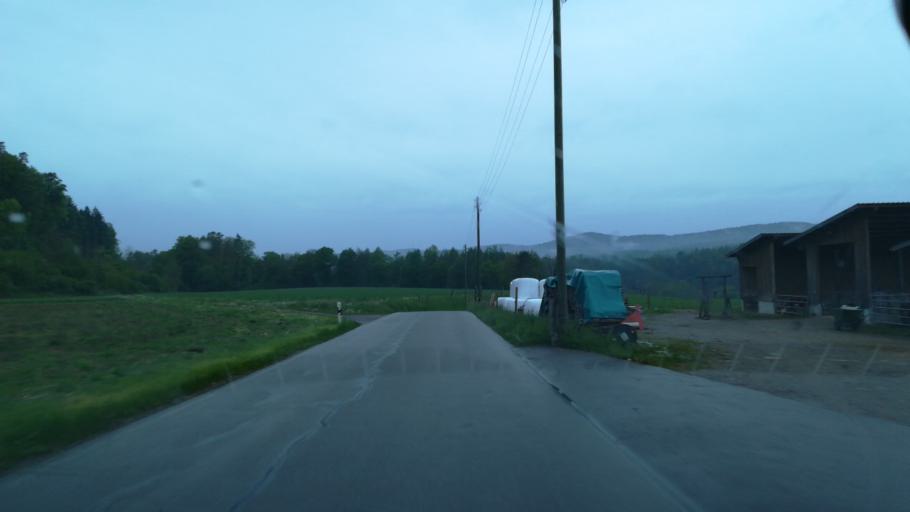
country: CH
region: Zurich
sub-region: Bezirk Buelach
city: Seglingen
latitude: 47.5767
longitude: 8.5035
